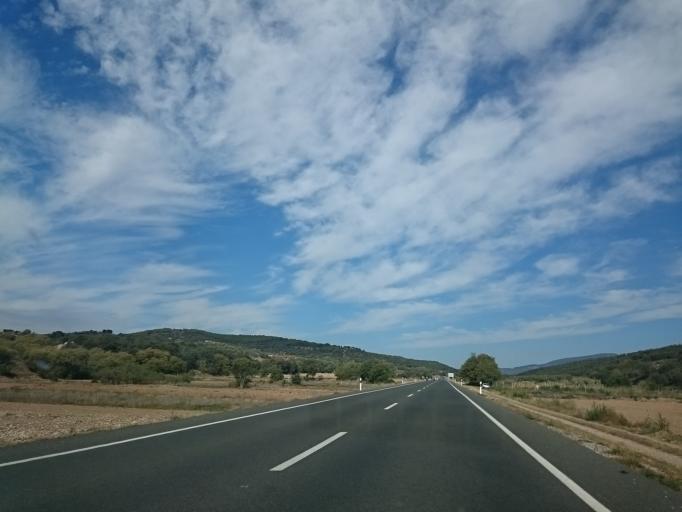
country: ES
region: Aragon
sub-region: Provincia de Huesca
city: Baells
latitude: 41.9153
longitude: 0.4702
